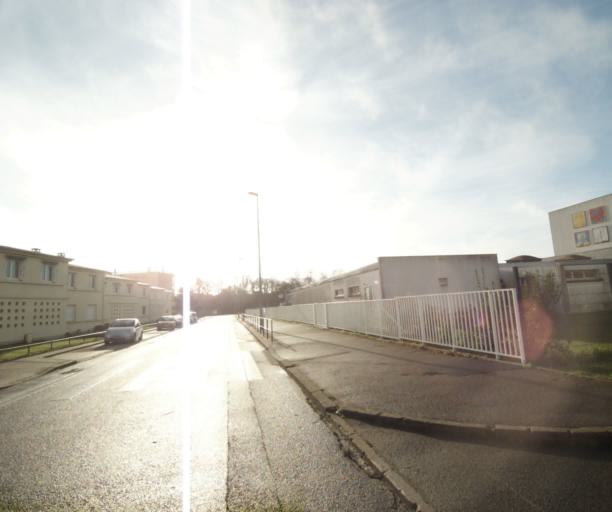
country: FR
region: Pays de la Loire
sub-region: Departement de la Sarthe
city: Le Mans
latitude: 47.9879
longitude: 0.2159
